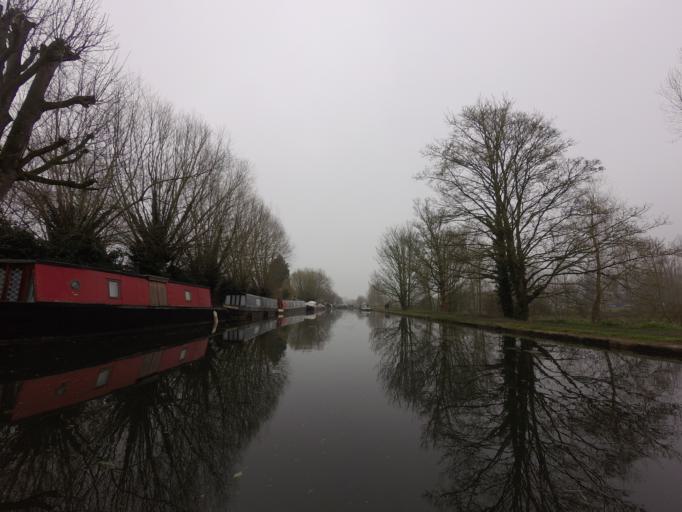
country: GB
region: England
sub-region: Hertfordshire
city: Hemel Hempstead
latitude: 51.7443
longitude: -0.4940
